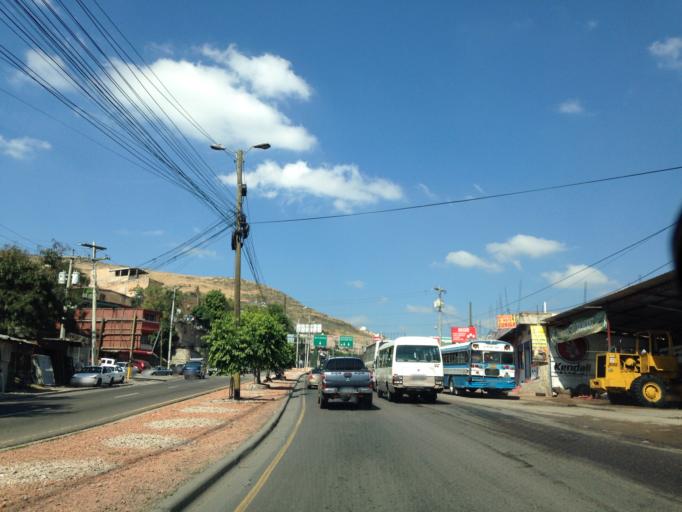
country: HN
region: Francisco Morazan
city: El Lolo
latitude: 14.1040
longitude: -87.2416
